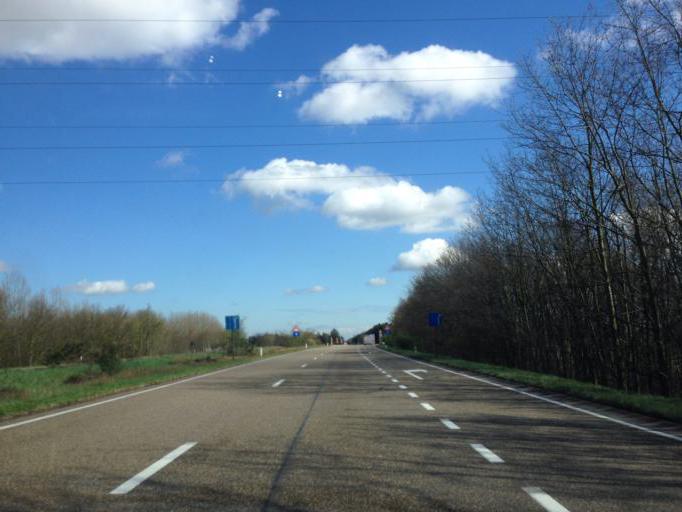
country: BE
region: Flanders
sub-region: Provincie Limburg
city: Overpelt
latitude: 51.2128
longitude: 5.3968
